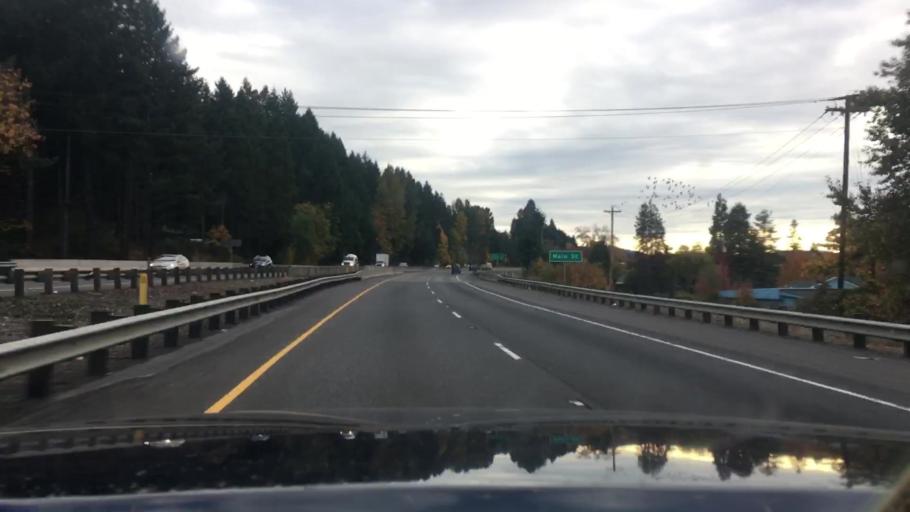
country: US
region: Oregon
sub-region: Lane County
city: Cottage Grove
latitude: 43.7983
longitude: -123.0460
